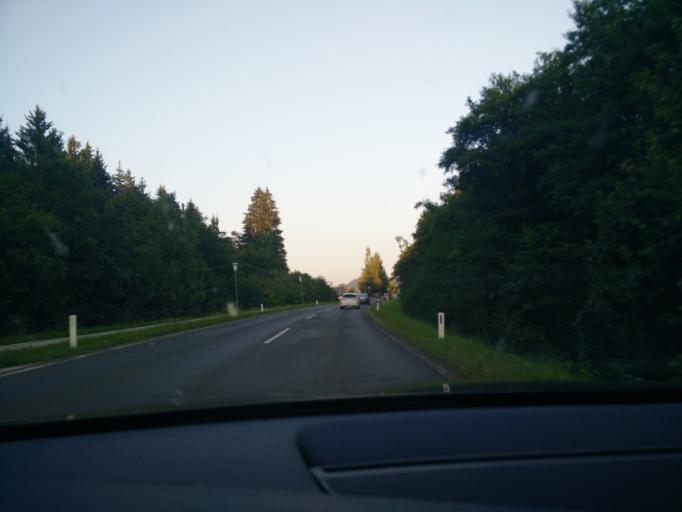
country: AT
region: Carinthia
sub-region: Politischer Bezirk Villach Land
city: Wernberg
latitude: 46.5893
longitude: 13.9038
